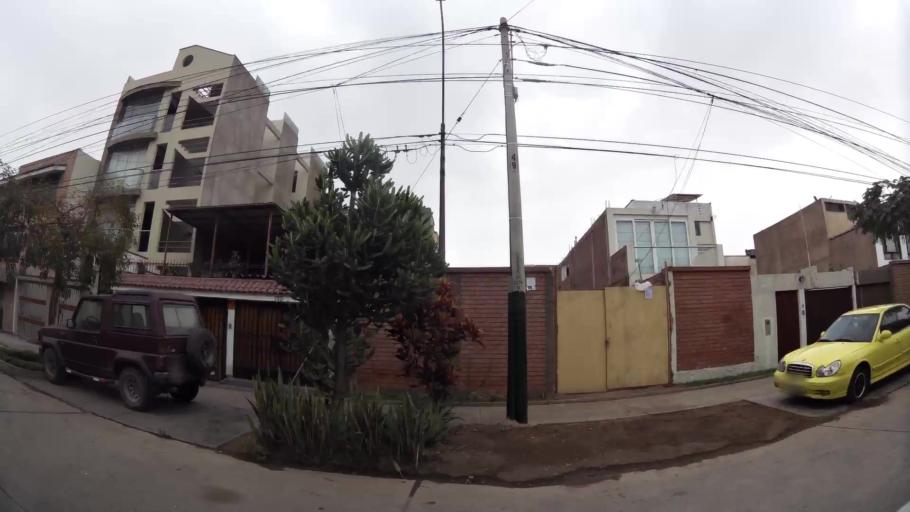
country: PE
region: Lima
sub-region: Lima
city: Surco
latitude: -12.1345
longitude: -76.9868
